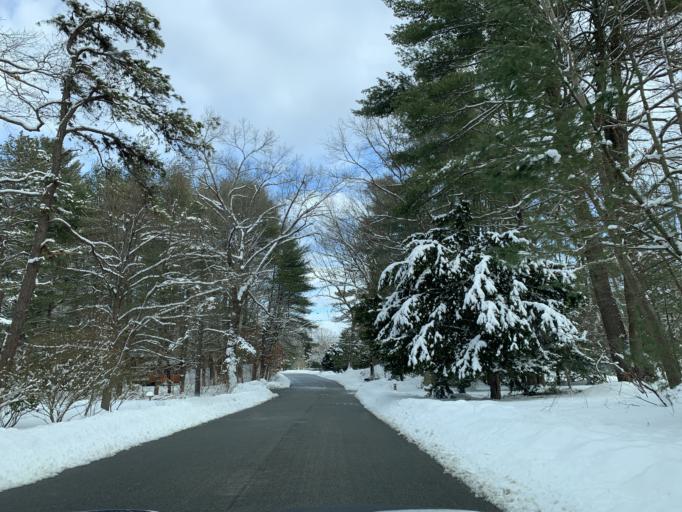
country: US
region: Massachusetts
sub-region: Norfolk County
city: Dover
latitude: 42.2570
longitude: -71.2932
